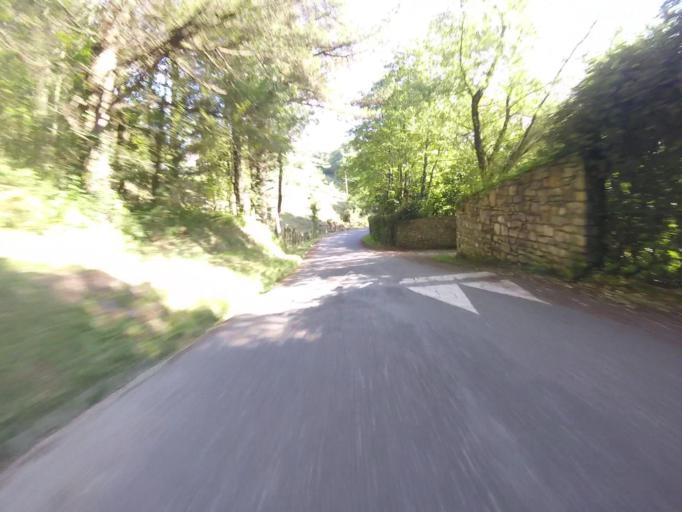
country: ES
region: Basque Country
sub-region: Provincia de Guipuzcoa
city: Astigarraga
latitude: 43.2664
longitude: -1.9296
